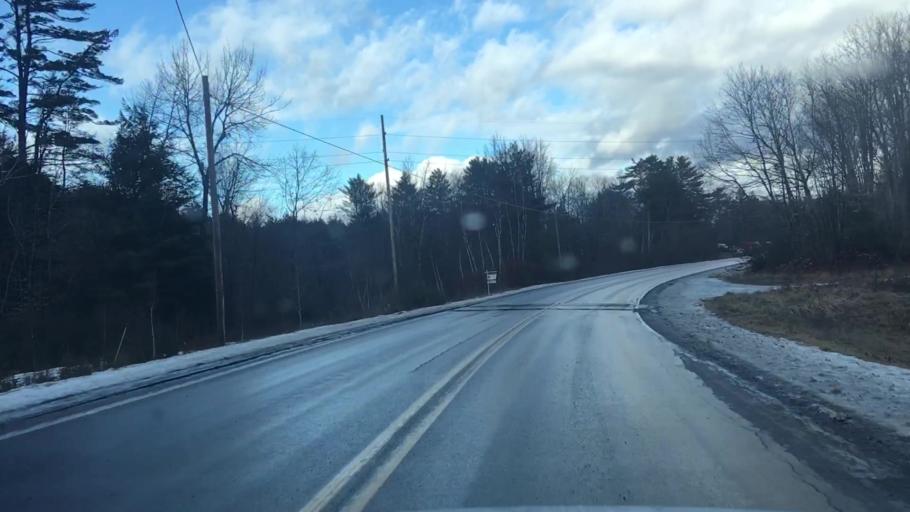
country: US
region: Maine
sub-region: Hancock County
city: Dedham
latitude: 44.6462
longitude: -68.6915
